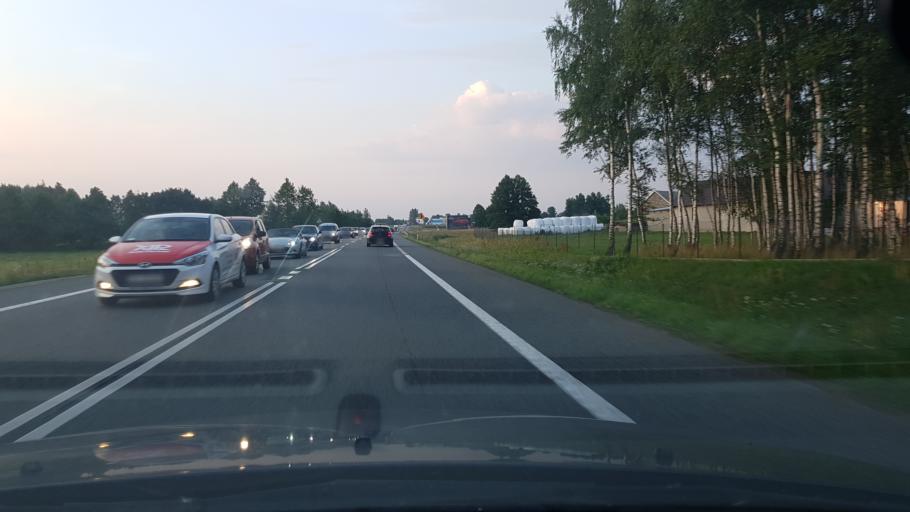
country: PL
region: Masovian Voivodeship
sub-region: Powiat mlawski
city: Wieczfnia Koscielna
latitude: 53.1883
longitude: 20.4316
